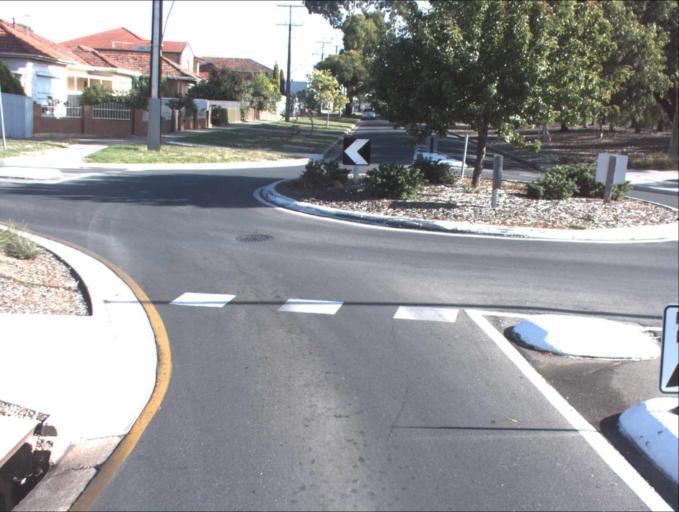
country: AU
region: South Australia
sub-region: Charles Sturt
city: Woodville North
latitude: -34.8607
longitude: 138.5519
